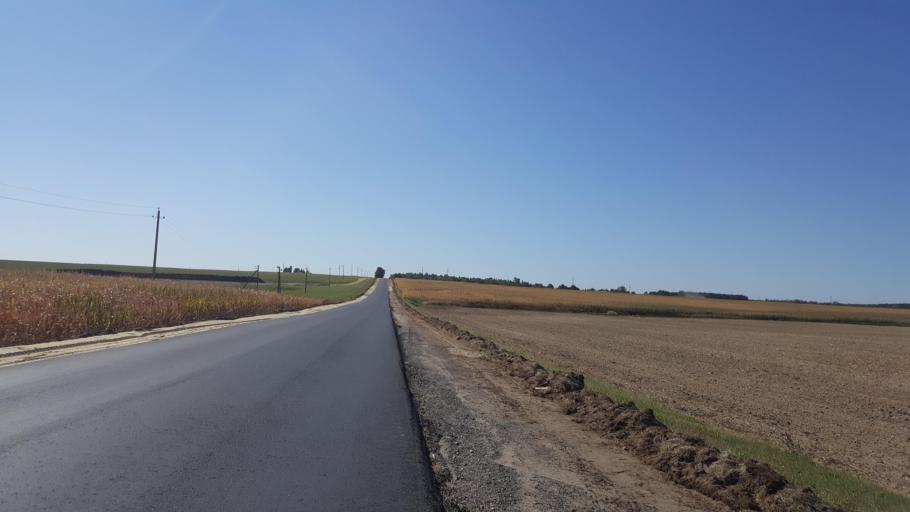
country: BY
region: Brest
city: Charnawchytsy
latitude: 52.2934
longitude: 23.6059
